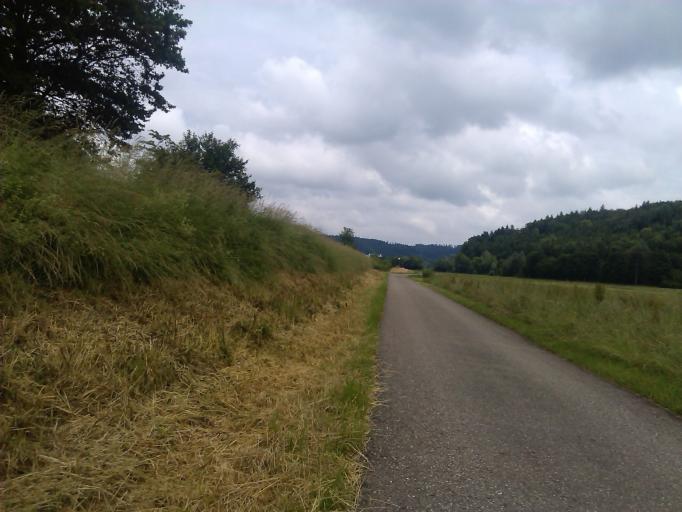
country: DE
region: Baden-Wuerttemberg
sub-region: Regierungsbezirk Stuttgart
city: Gaildorf
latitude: 48.9663
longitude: 9.8277
